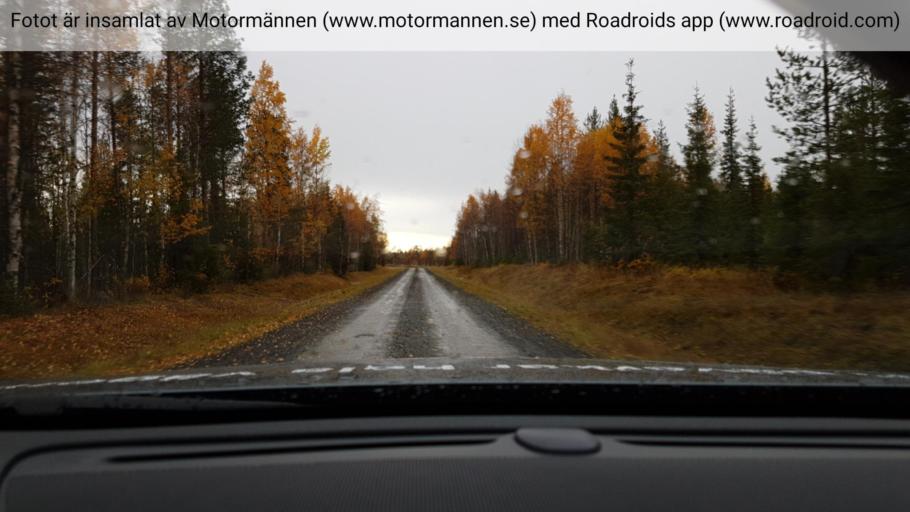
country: SE
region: Norrbotten
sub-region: Pajala Kommun
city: Pajala
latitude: 67.0651
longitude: 22.8263
